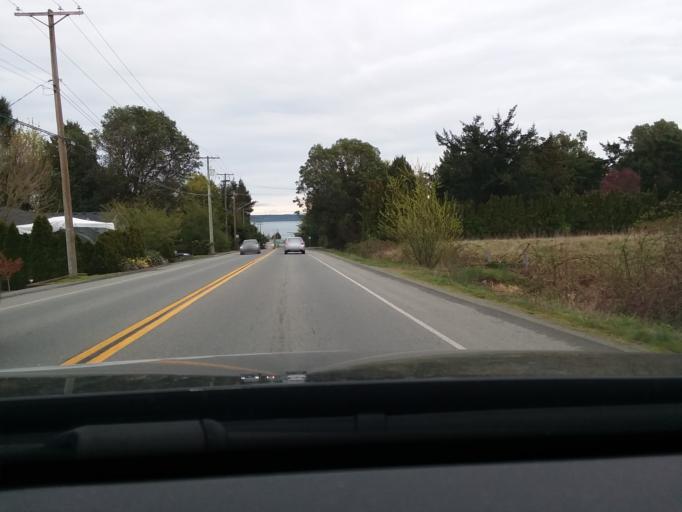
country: CA
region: British Columbia
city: North Saanich
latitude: 48.6300
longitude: -123.4181
